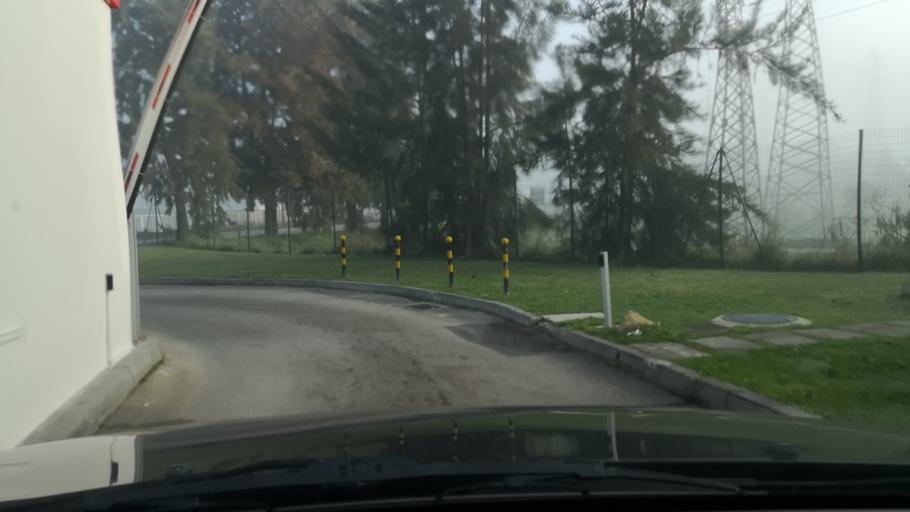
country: PT
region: Setubal
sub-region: Setubal
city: Setubal
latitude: 38.5352
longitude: -8.8623
